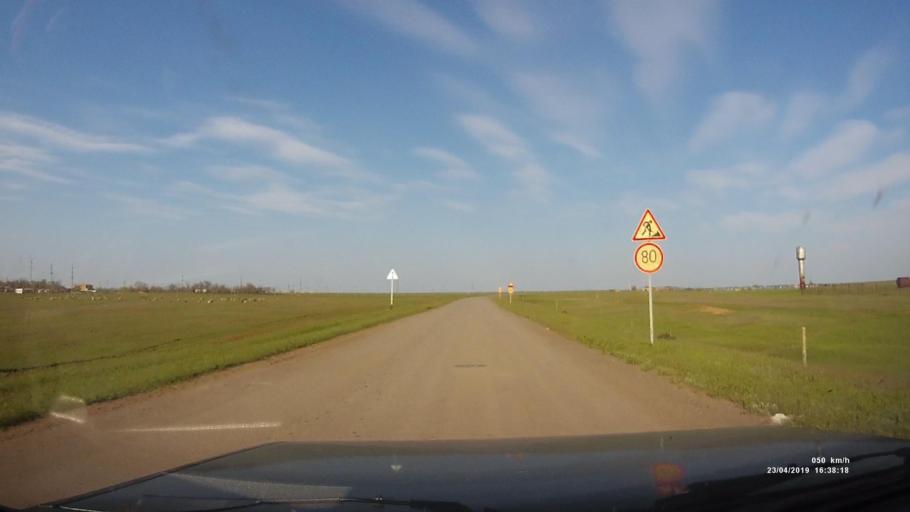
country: RU
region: Kalmykiya
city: Priyutnoye
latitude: 46.3346
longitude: 43.1524
